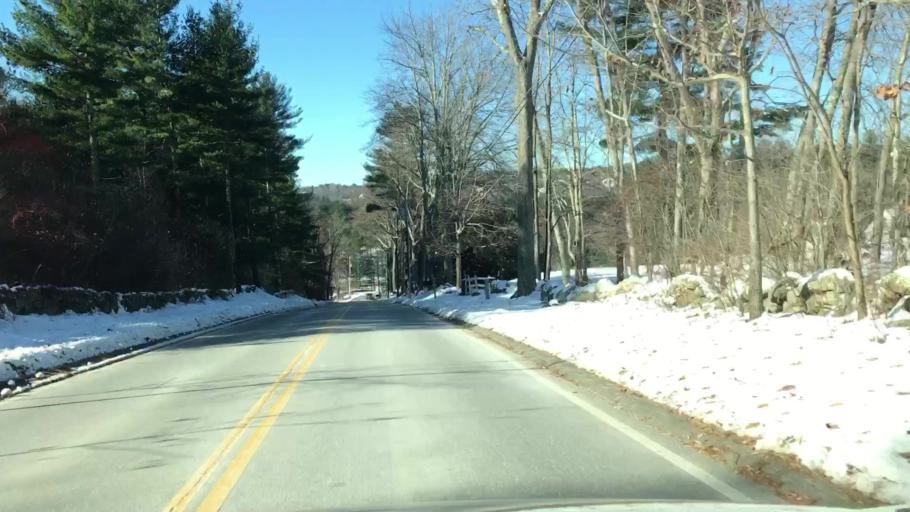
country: US
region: New Hampshire
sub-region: Hillsborough County
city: Bedford
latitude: 42.9243
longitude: -71.5748
